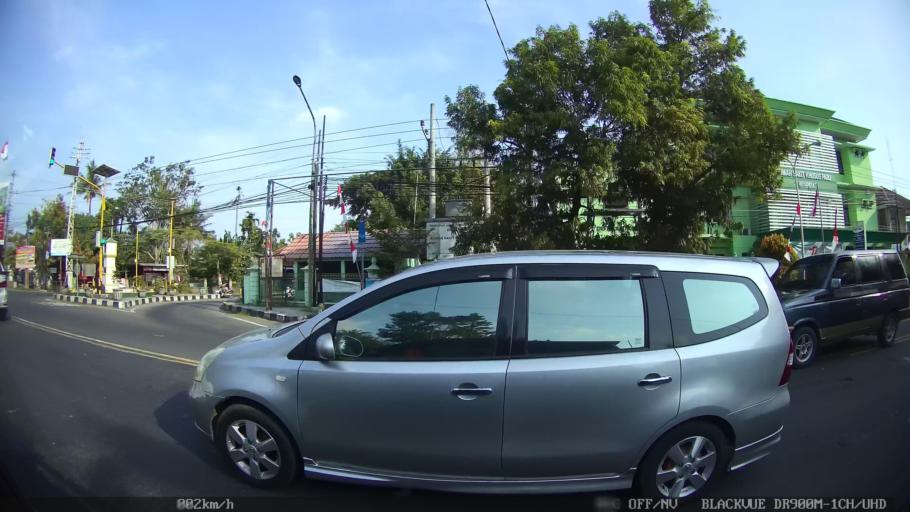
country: ID
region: Daerah Istimewa Yogyakarta
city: Bantul
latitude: -7.9053
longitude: 110.3206
